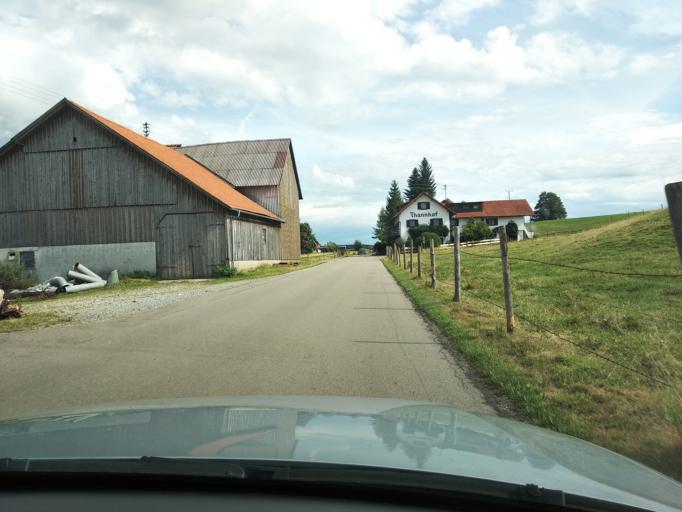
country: DE
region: Bavaria
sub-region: Swabia
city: Woringen
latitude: 47.8887
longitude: 10.2271
